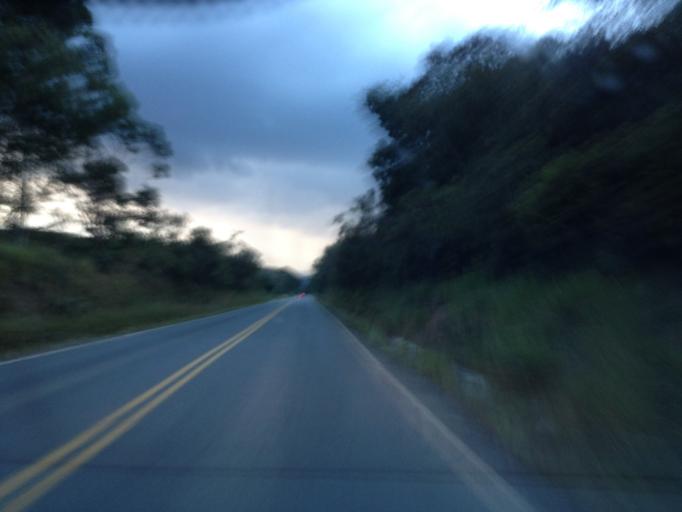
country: BR
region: Minas Gerais
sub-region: Caxambu
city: Caxambu
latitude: -22.0222
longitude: -45.0165
